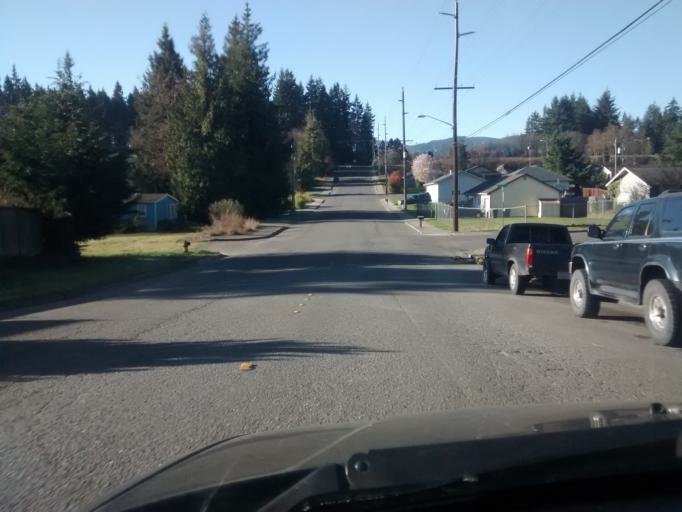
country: US
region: Washington
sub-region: Clallam County
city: Port Angeles
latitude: 48.1203
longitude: -123.4734
